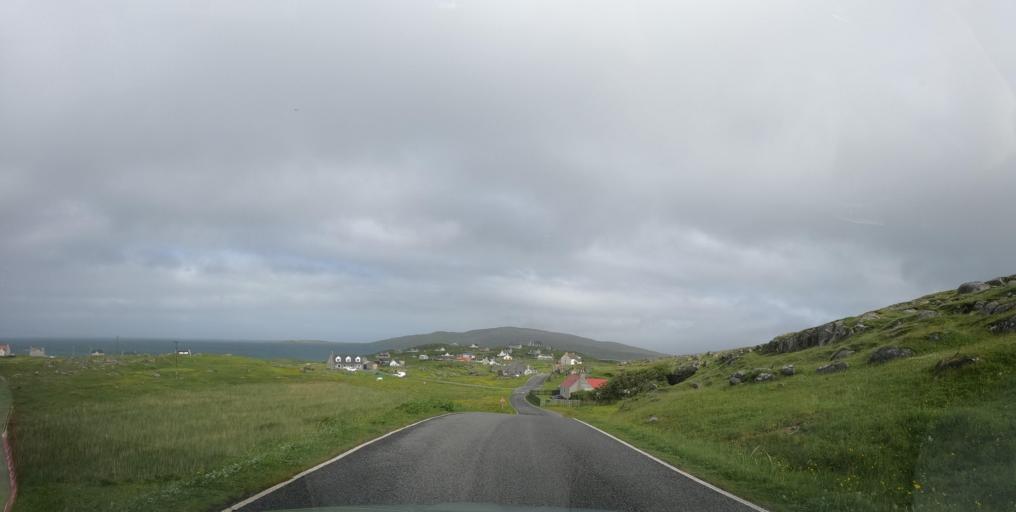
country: GB
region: Scotland
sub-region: Eilean Siar
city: Isle of South Uist
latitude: 57.0807
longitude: -7.3030
